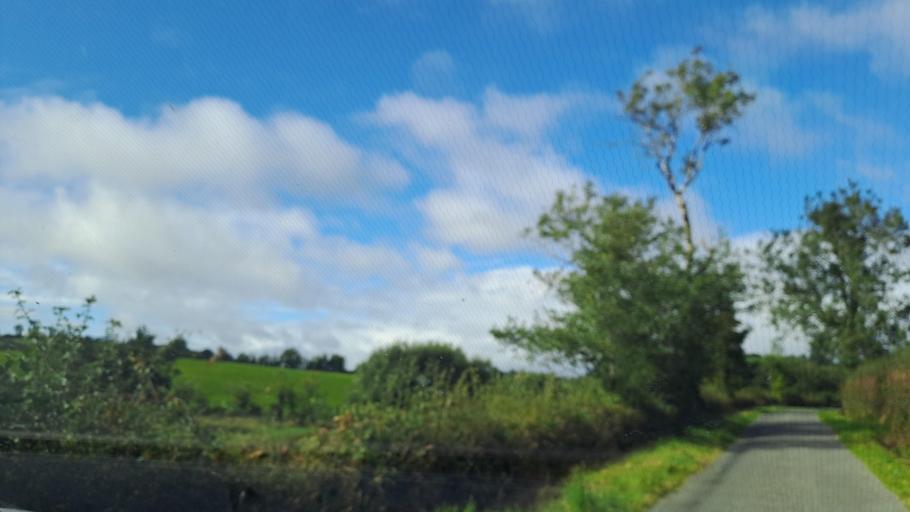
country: IE
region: Ulster
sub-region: An Cabhan
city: Kingscourt
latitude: 53.9708
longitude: -6.8602
